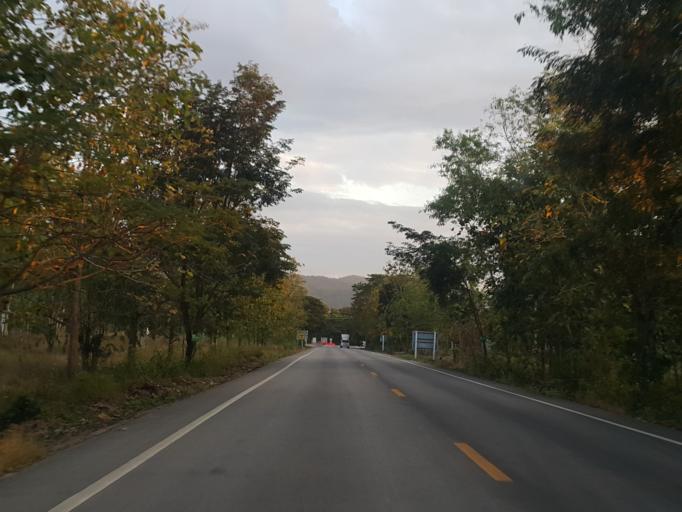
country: TH
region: Lampang
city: Mae Mo
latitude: 18.4192
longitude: 99.6484
